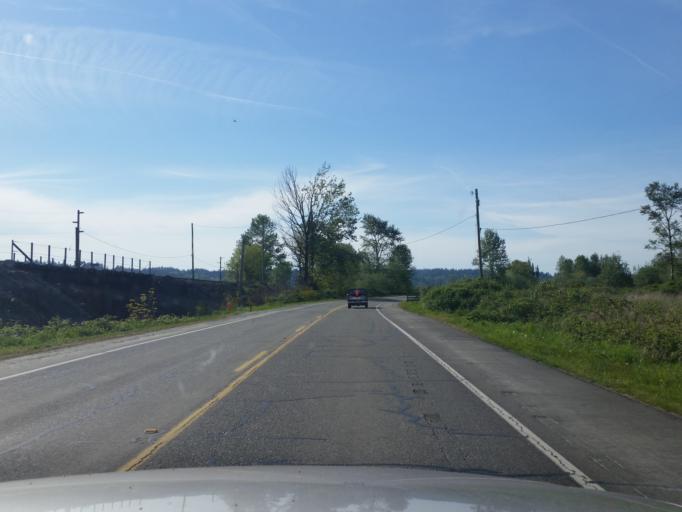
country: US
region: Washington
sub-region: Snohomish County
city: Fobes Hill
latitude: 47.9209
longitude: -122.1491
